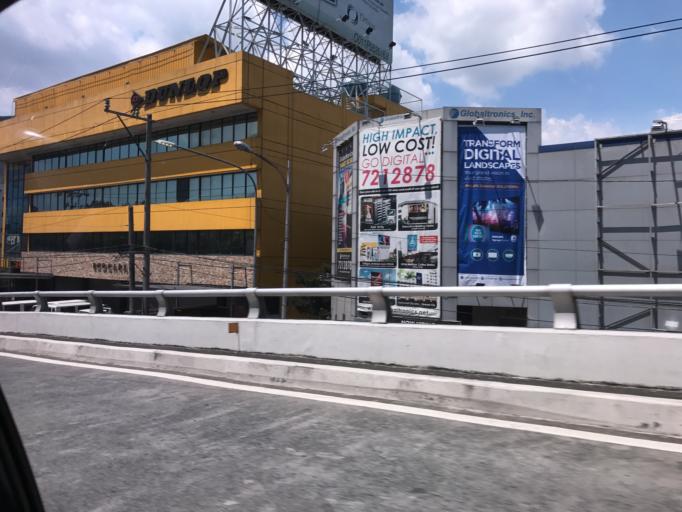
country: PH
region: Metro Manila
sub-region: Pasig
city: Pasig City
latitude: 14.5945
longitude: 121.0567
